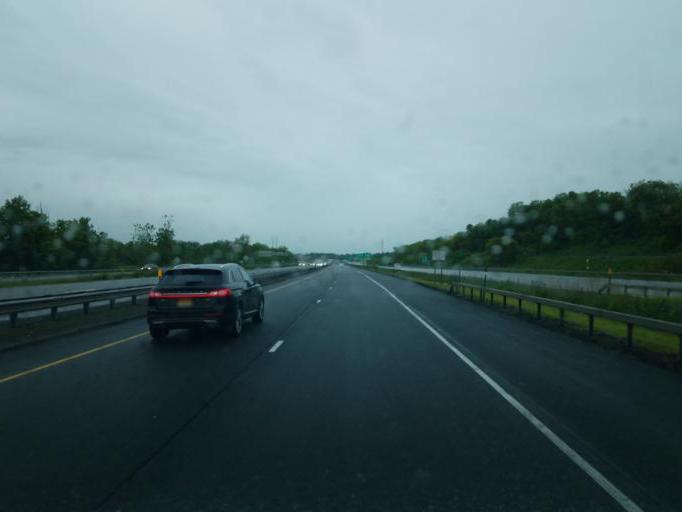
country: US
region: New York
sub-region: Oneida County
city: Utica
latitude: 43.1168
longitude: -75.2165
